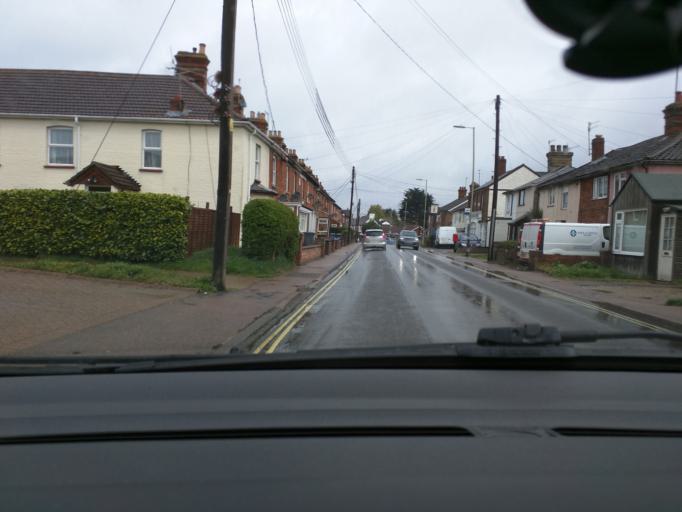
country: GB
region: England
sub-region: Suffolk
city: Leiston
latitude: 52.2032
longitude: 1.5740
